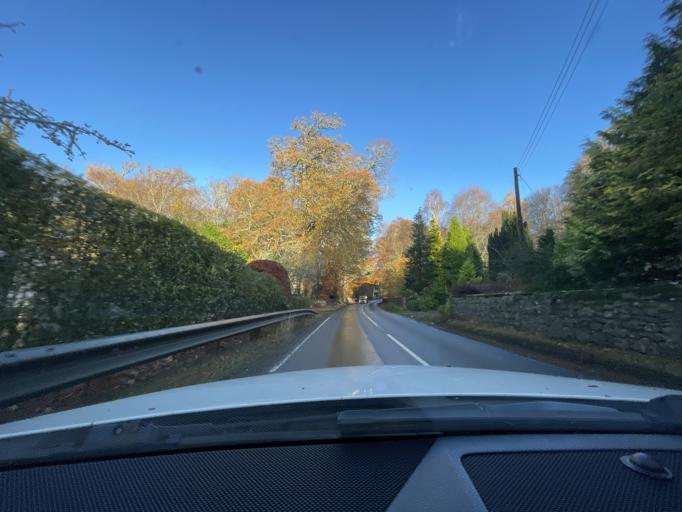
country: GB
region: Scotland
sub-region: Highland
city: Inverness
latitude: 57.4420
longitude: -4.2624
